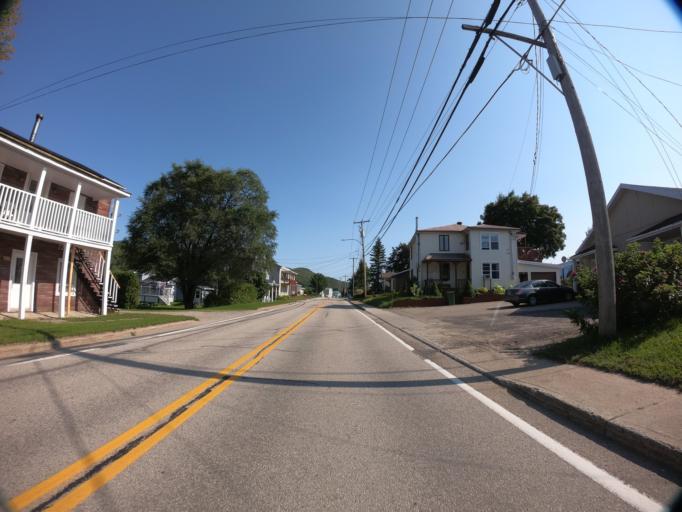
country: CA
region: Quebec
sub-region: Capitale-Nationale
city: Baie-Saint-Paul
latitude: 47.5537
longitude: -70.5341
